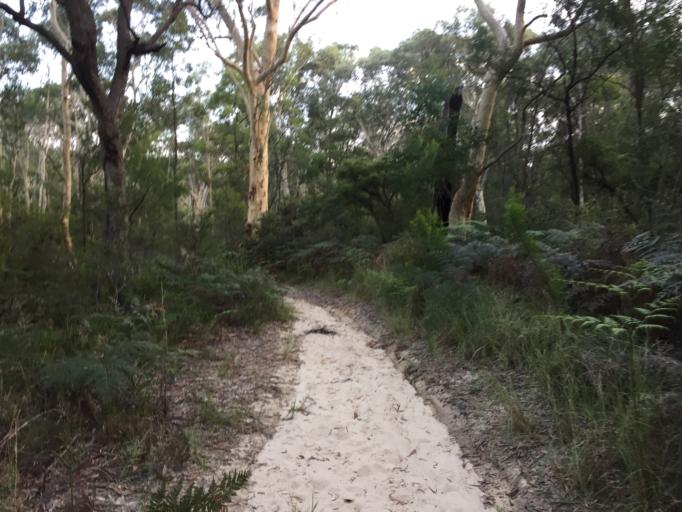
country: AU
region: New South Wales
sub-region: Blue Mountains Municipality
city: Blaxland
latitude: -33.7339
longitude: 150.6200
